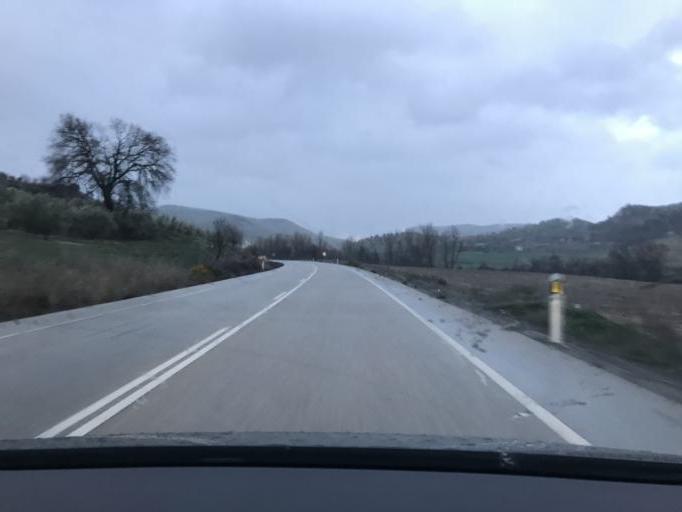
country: ES
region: Andalusia
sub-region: Provincia de Granada
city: Campotejar
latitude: 37.4485
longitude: -3.6425
